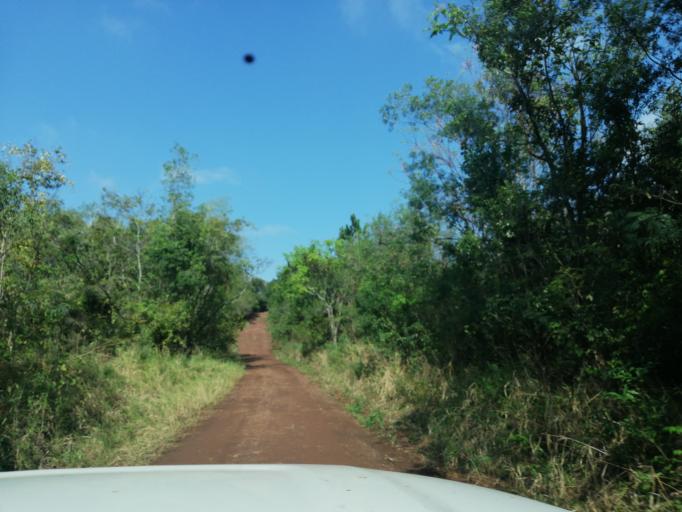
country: AR
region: Misiones
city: Cerro Azul
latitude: -27.6171
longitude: -55.5227
